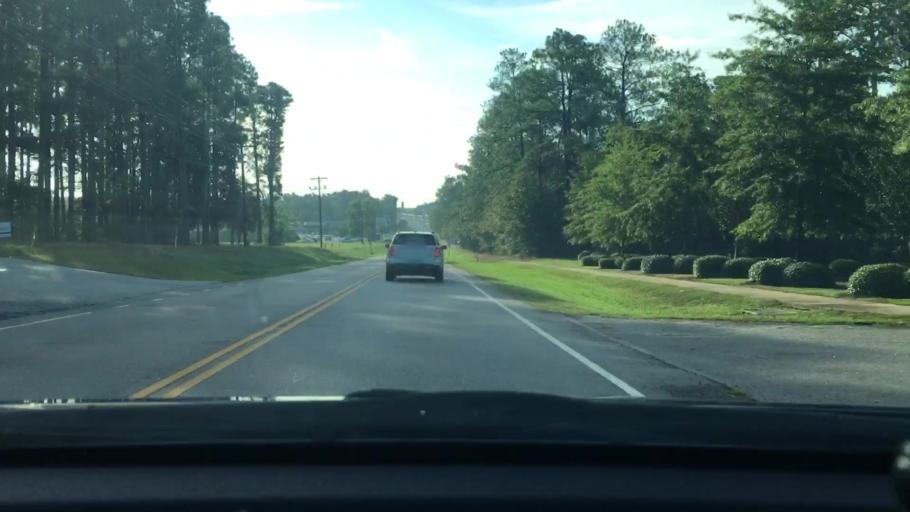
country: US
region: South Carolina
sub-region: Lexington County
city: Irmo
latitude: 34.1047
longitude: -81.1858
